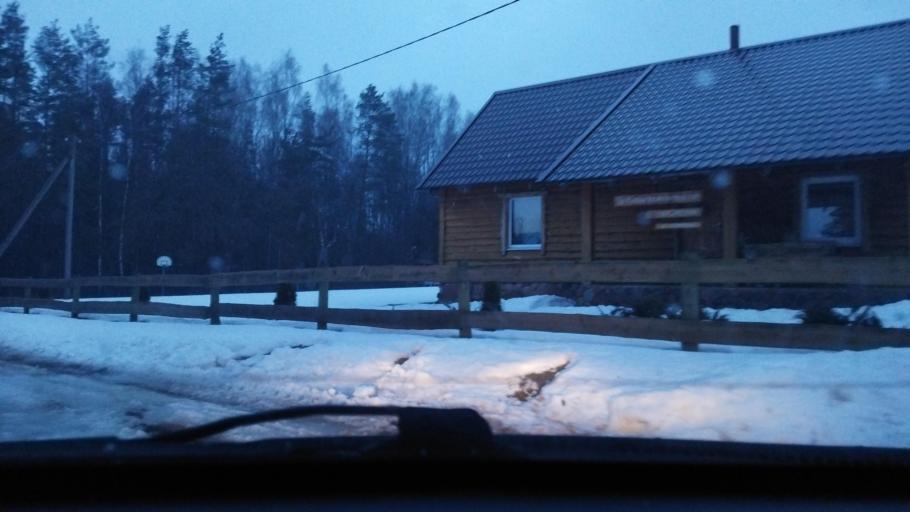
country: BY
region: Minsk
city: Svir
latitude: 54.9399
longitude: 26.4053
